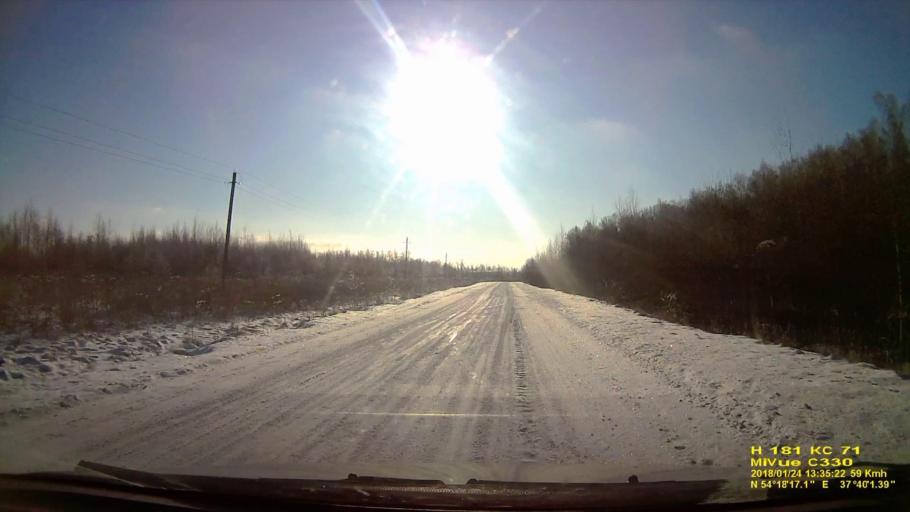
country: RU
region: Tula
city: Revyakino
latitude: 54.3046
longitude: 37.6670
